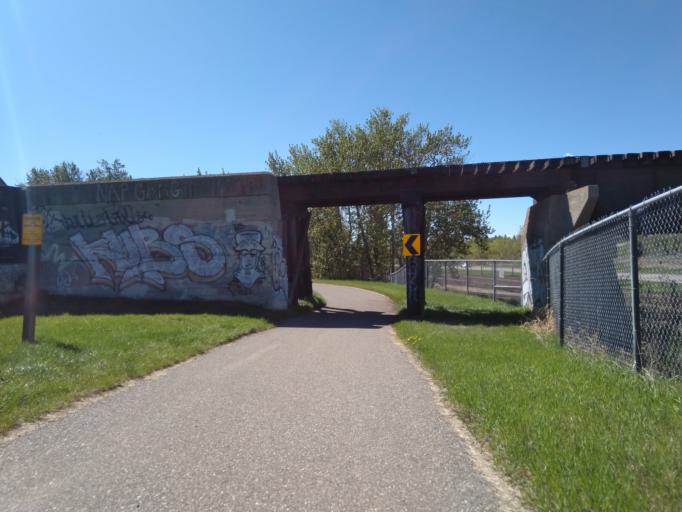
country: CA
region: Alberta
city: Calgary
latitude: 51.0030
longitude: -114.0115
